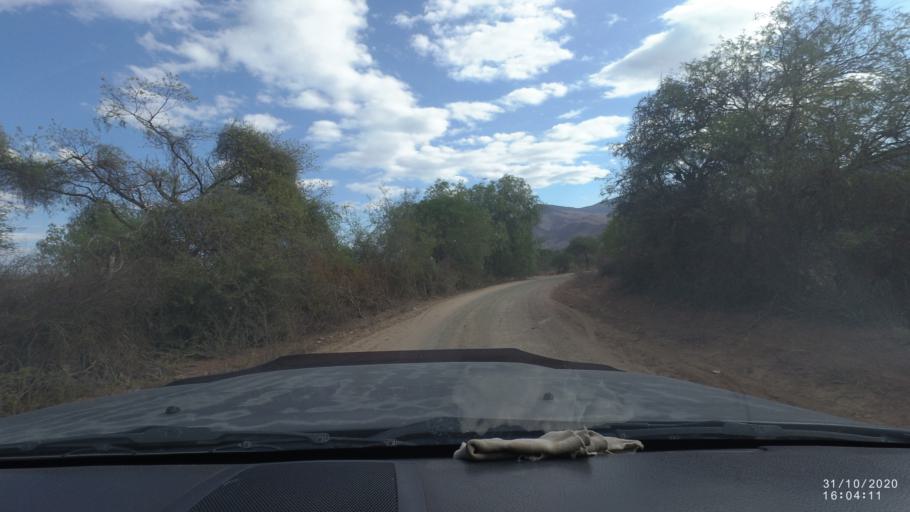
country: BO
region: Chuquisaca
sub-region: Provincia Zudanez
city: Mojocoya
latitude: -18.3581
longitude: -64.6506
